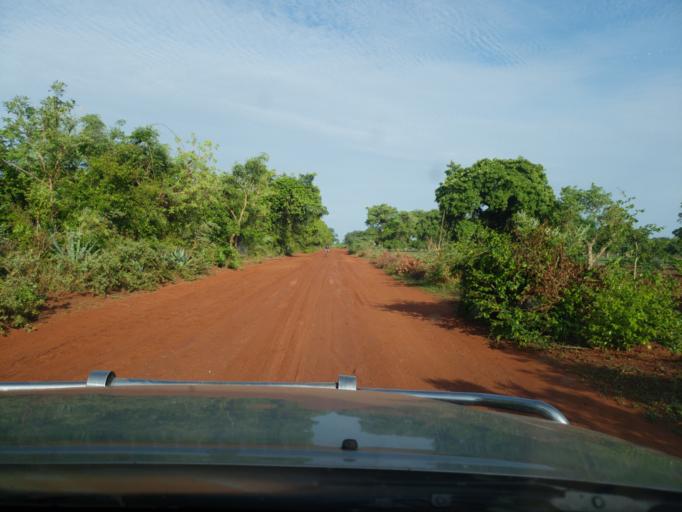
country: ML
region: Sikasso
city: Koutiala
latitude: 12.4245
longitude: -5.6599
